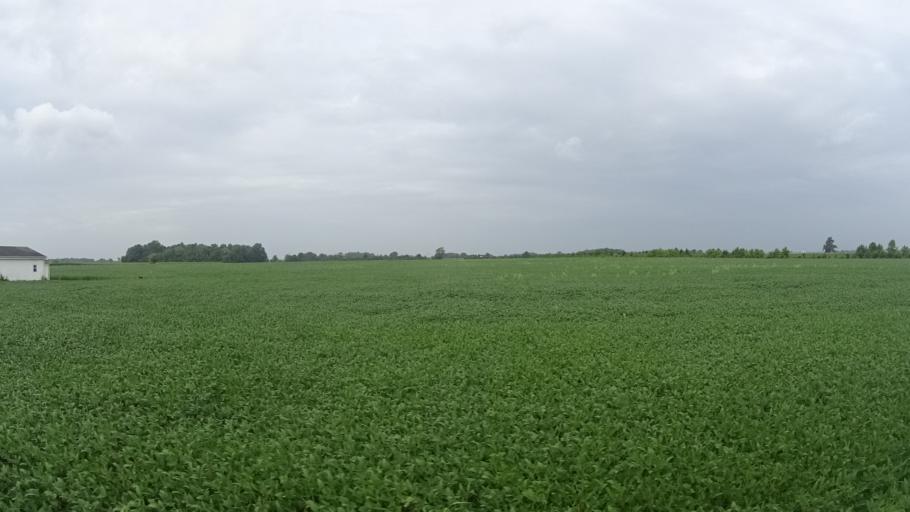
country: US
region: Indiana
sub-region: Madison County
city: Lapel
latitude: 40.0270
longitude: -85.8055
